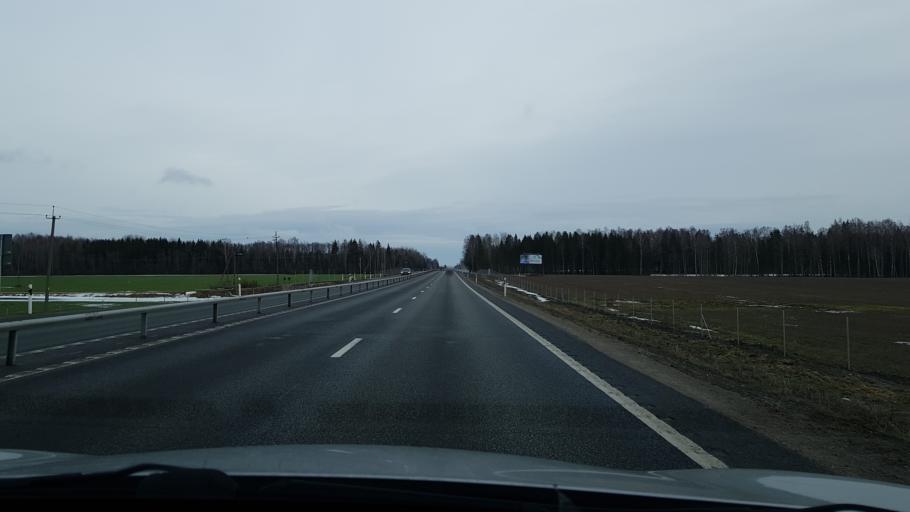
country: EE
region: Tartu
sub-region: Puhja vald
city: Puhja
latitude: 58.4622
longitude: 26.3879
